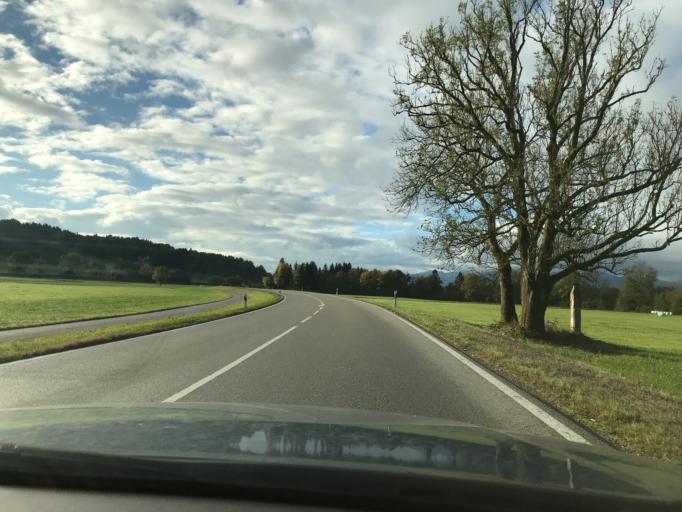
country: DE
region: Bavaria
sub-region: Upper Bavaria
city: Konigsdorf
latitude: 47.8339
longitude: 11.5308
